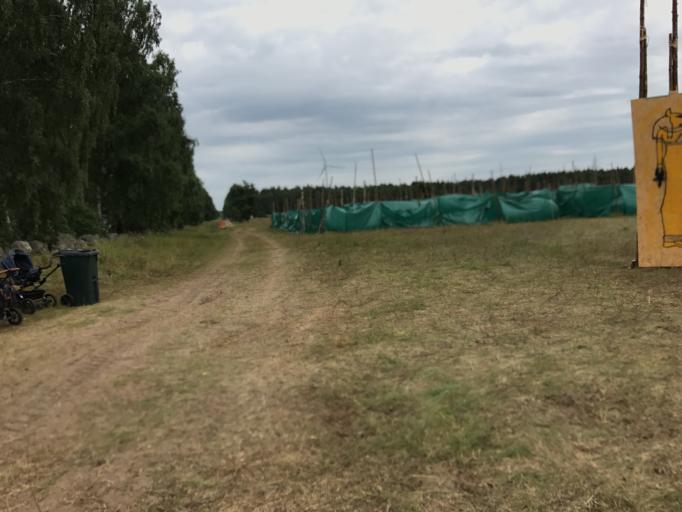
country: SE
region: Skane
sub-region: Kristianstads Kommun
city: Fjalkinge
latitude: 56.0057
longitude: 14.3102
